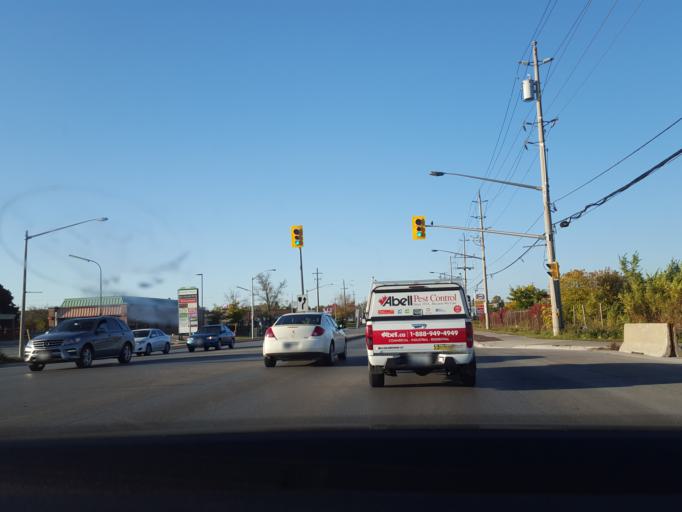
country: CA
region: Ontario
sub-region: York
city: Richmond Hill
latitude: 43.8841
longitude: -79.4401
